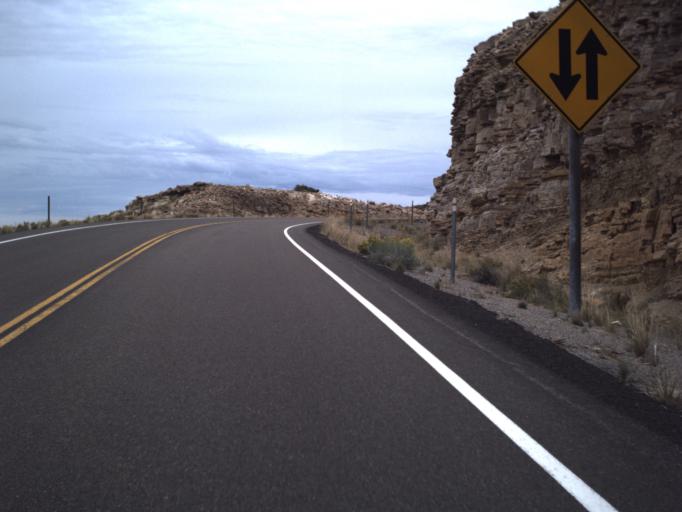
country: US
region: Utah
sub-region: Emery County
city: Castle Dale
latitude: 38.9347
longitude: -110.4751
